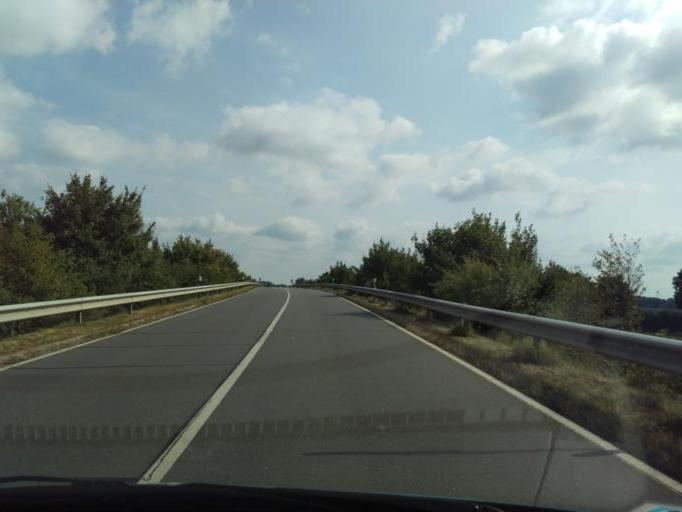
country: DE
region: Lower Saxony
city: Dollbergen
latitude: 52.4152
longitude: 10.1691
